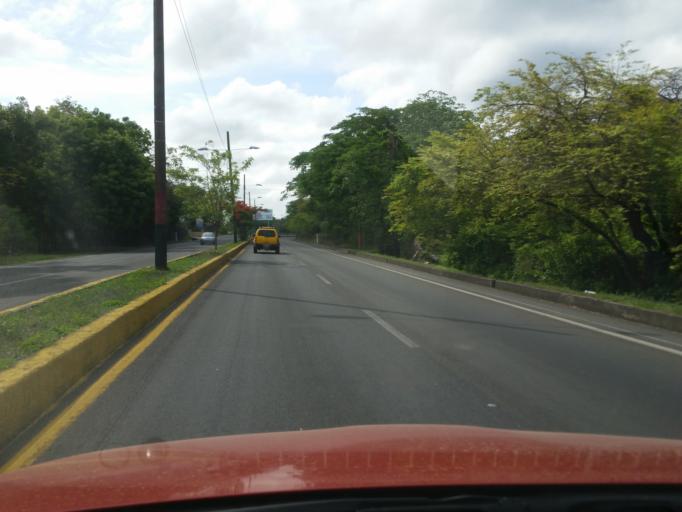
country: NI
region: Masaya
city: Nindiri
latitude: 12.0195
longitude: -86.1488
